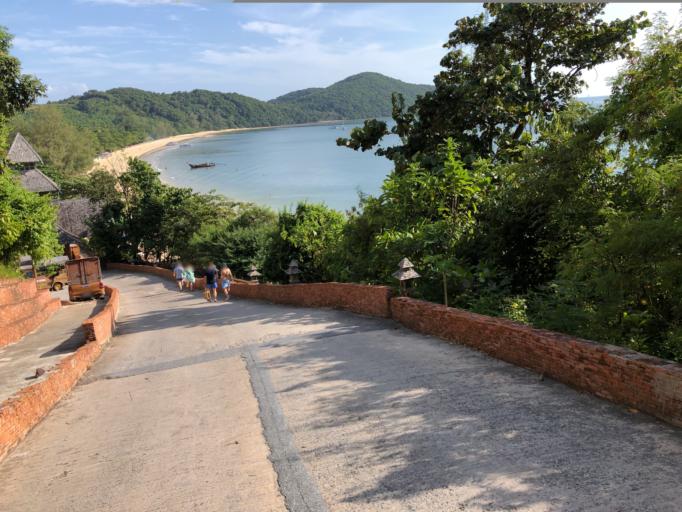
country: TH
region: Phangnga
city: Ban Phru Nai
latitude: 7.9833
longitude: 98.5677
